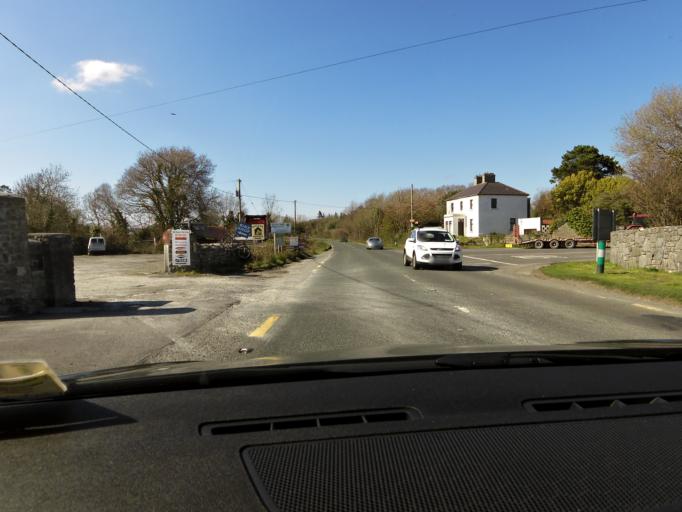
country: IE
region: Connaught
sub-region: County Galway
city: Moycullen
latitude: 53.3554
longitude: -9.2070
